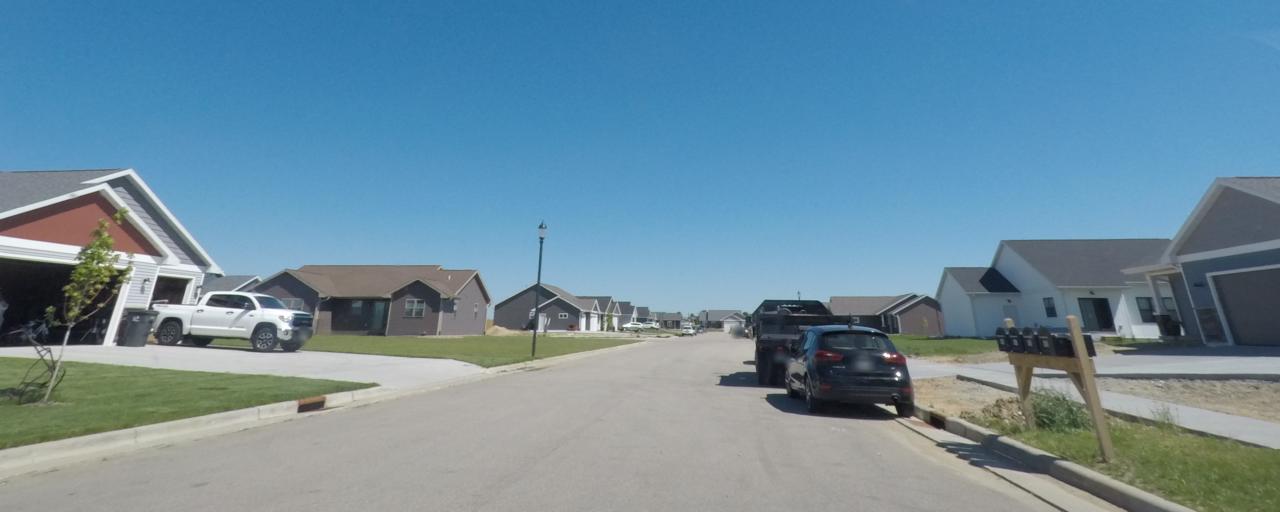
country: US
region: Wisconsin
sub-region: Rock County
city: Evansville
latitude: 42.7736
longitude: -89.3211
